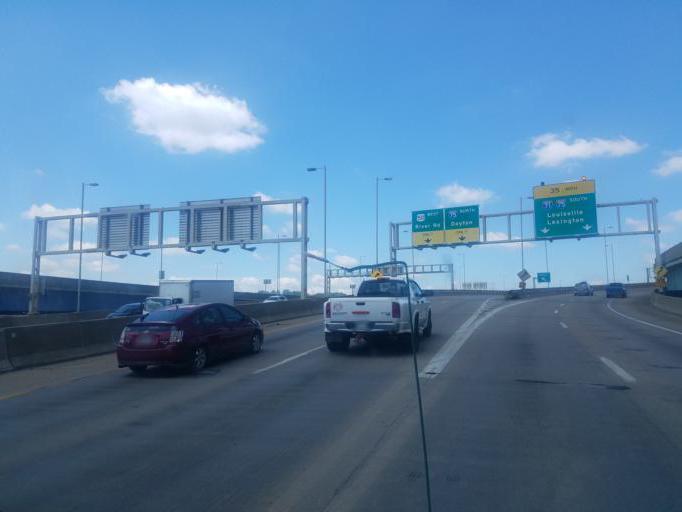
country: US
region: Kentucky
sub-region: Kenton County
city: Covington
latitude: 39.0980
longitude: -84.5170
